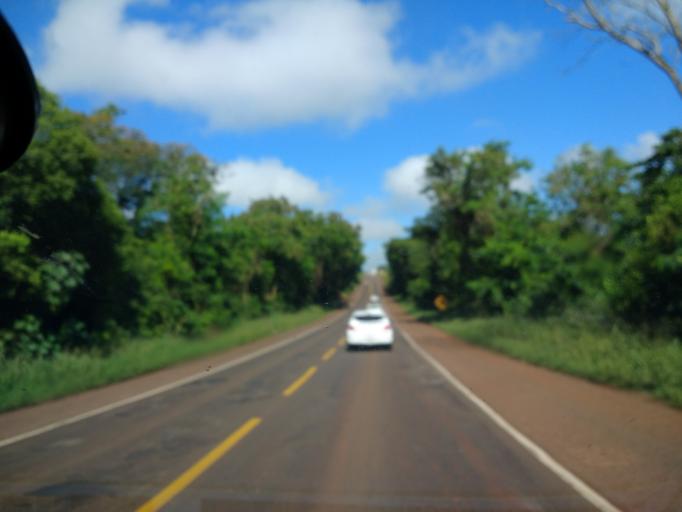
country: BR
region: Parana
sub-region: Paicandu
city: Paicandu
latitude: -23.5422
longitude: -52.2256
